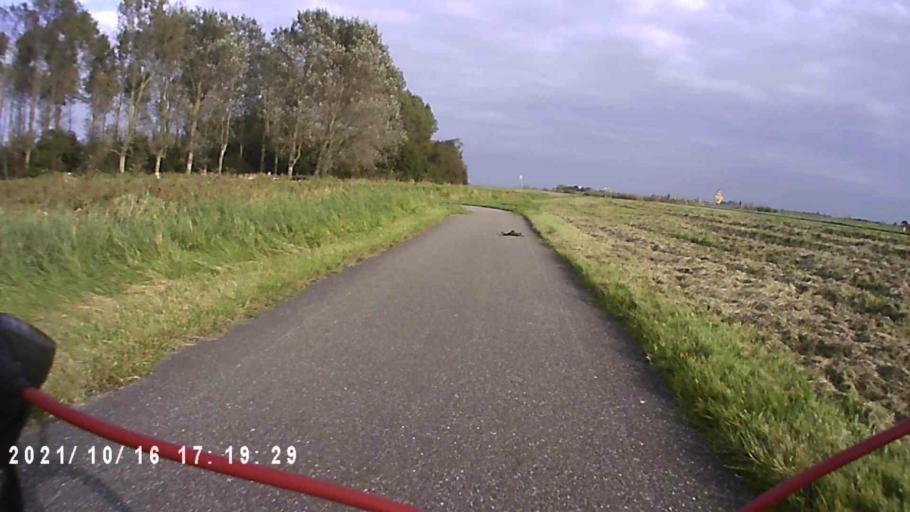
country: NL
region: Friesland
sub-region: Gemeente Kollumerland en Nieuwkruisland
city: Kollum
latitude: 53.3172
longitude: 6.1734
